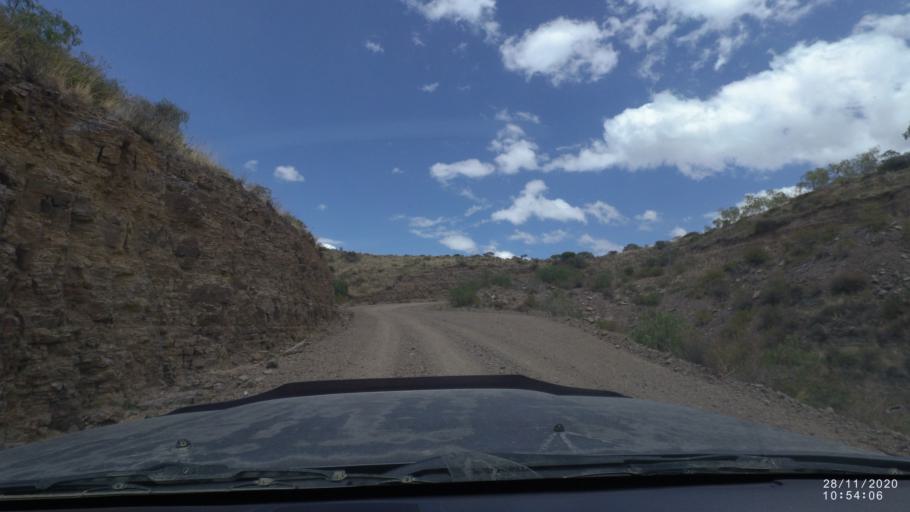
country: BO
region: Cochabamba
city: Capinota
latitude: -17.7786
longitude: -66.1196
